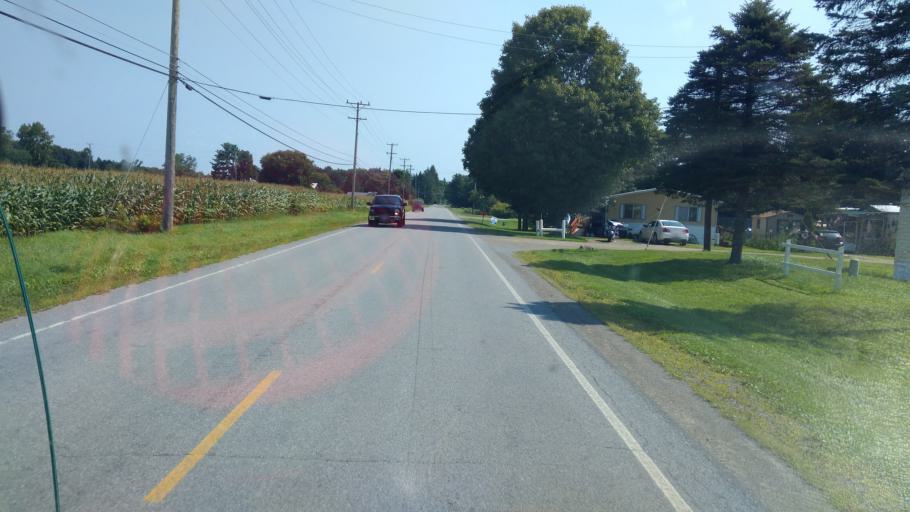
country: US
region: New York
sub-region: Allegany County
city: Friendship
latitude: 42.2176
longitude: -78.1071
